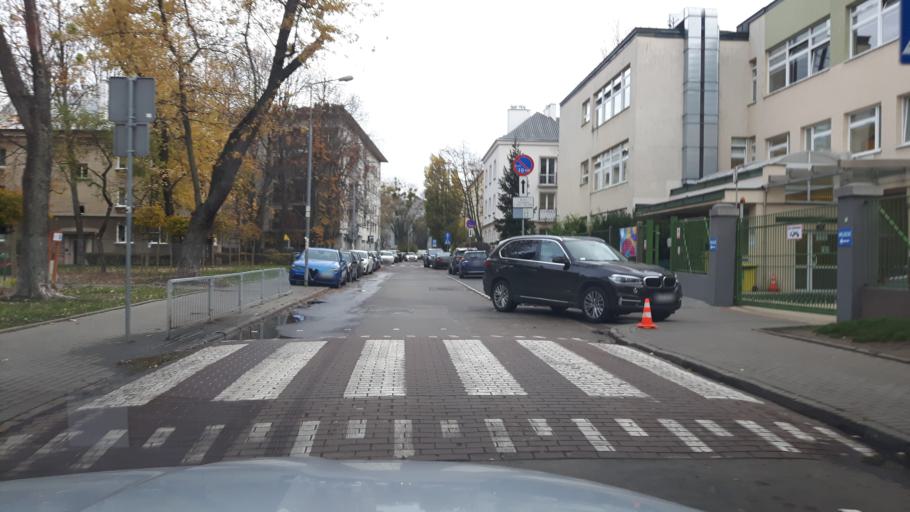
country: PL
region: Masovian Voivodeship
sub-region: Warszawa
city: Mokotow
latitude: 52.1725
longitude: 21.0001
